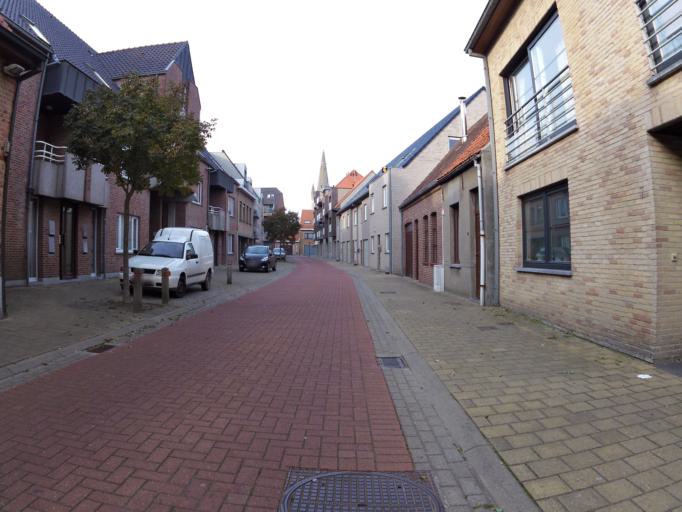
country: BE
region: Flanders
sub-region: Provincie West-Vlaanderen
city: Gistel
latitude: 51.1554
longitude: 2.9687
